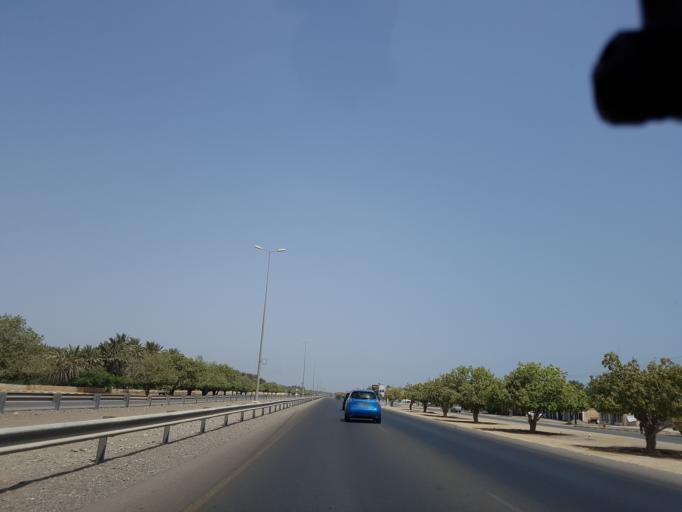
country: OM
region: Al Batinah
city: Saham
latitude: 24.1634
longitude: 56.8632
